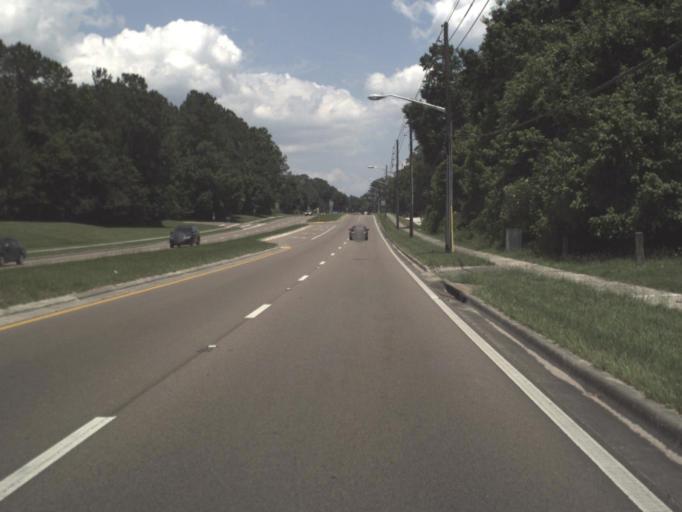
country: US
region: Florida
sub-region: Alachua County
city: Alachua
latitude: 29.6598
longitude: -82.4528
